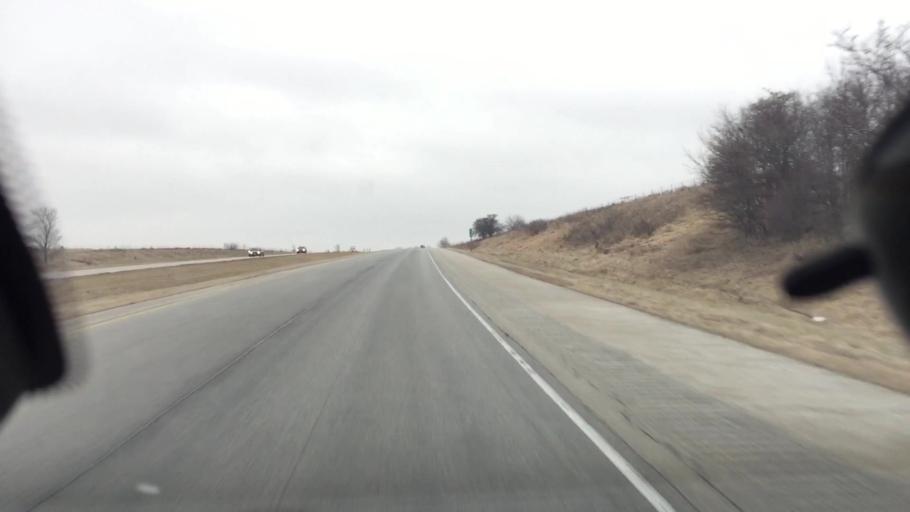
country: US
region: Illinois
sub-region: Henry County
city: Cambridge
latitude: 41.1507
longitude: -90.3313
